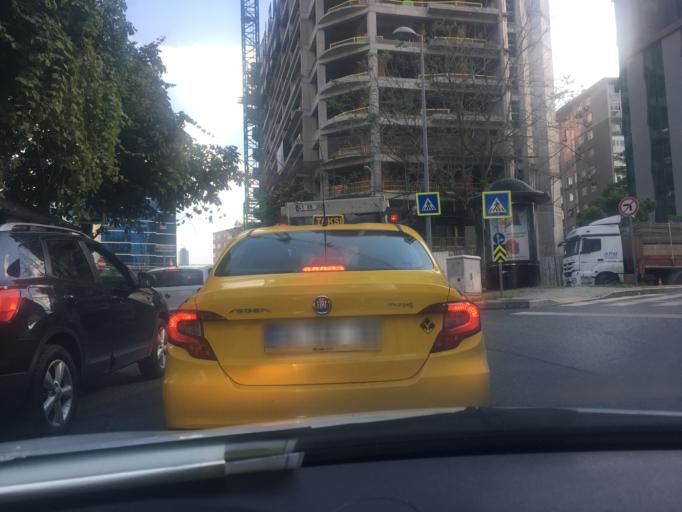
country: TR
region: Istanbul
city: Sisli
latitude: 41.0657
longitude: 29.0031
